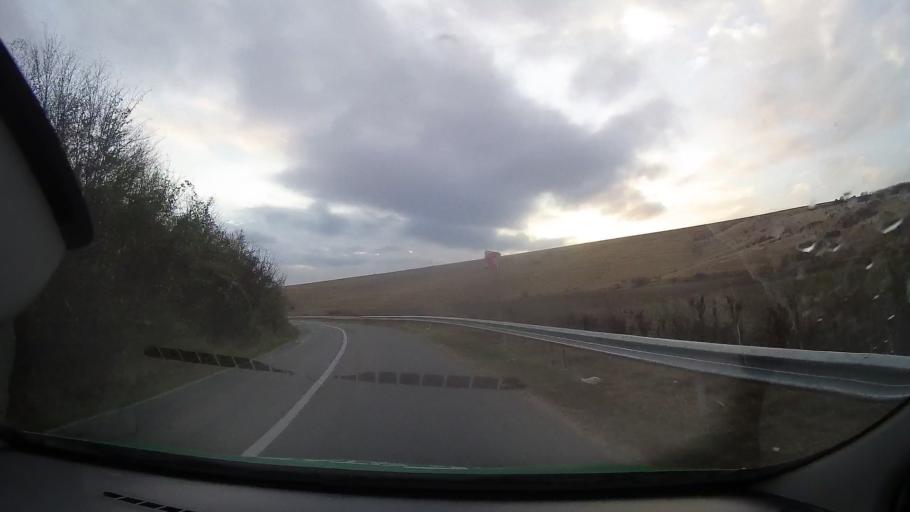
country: RO
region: Constanta
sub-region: Comuna Dobromir
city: Dobromir
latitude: 44.0378
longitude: 27.8040
